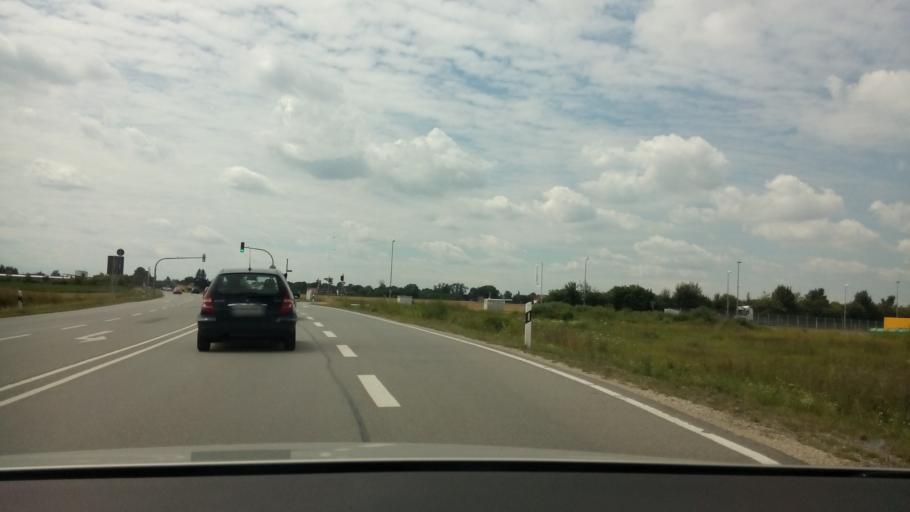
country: DE
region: Bavaria
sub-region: Upper Bavaria
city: Neufahrn bei Freising
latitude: 48.3285
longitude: 11.6941
